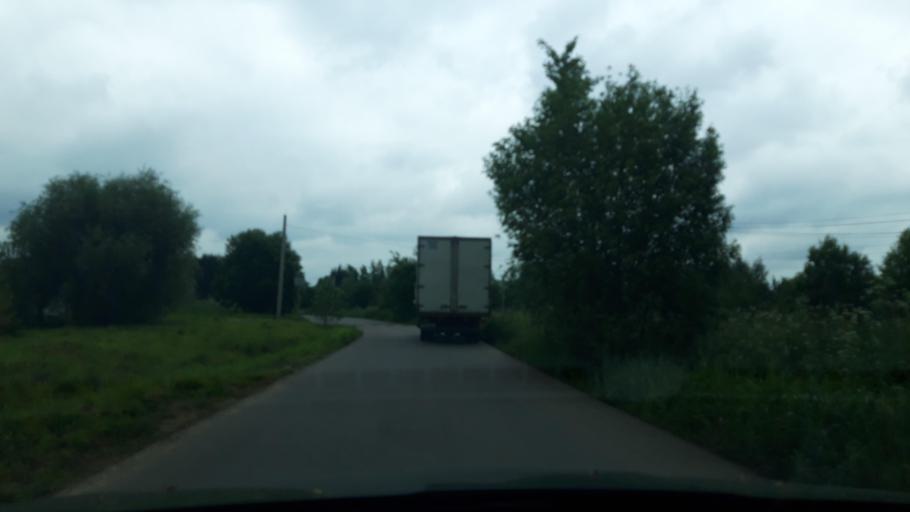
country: RU
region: Moskovskaya
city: Pavlovskaya Sloboda
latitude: 55.7747
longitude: 37.1051
